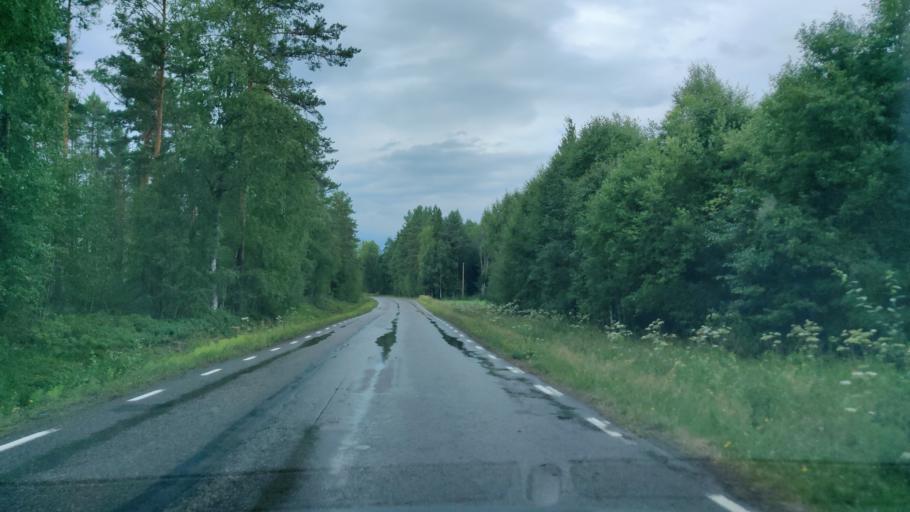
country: SE
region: Vaermland
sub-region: Munkfors Kommun
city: Munkfors
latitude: 59.8780
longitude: 13.5224
